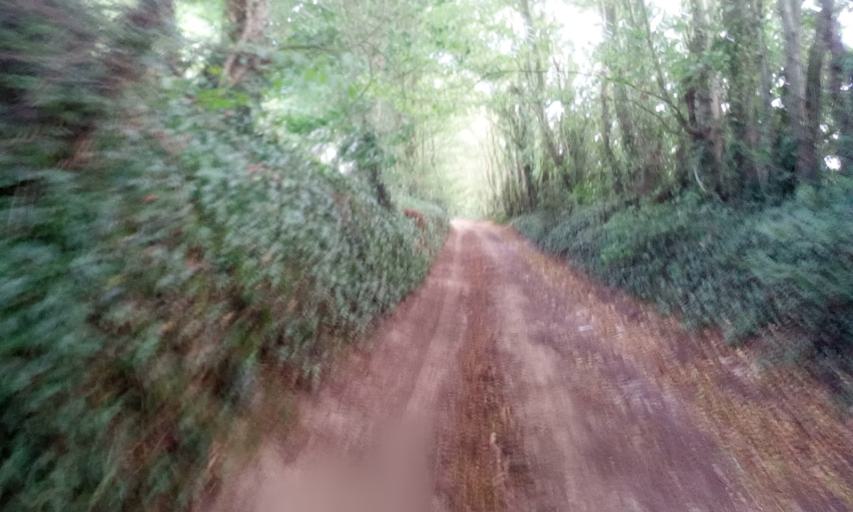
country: FR
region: Lower Normandy
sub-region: Departement du Calvados
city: Courseulles-sur-Mer
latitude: 49.2982
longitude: -0.4766
